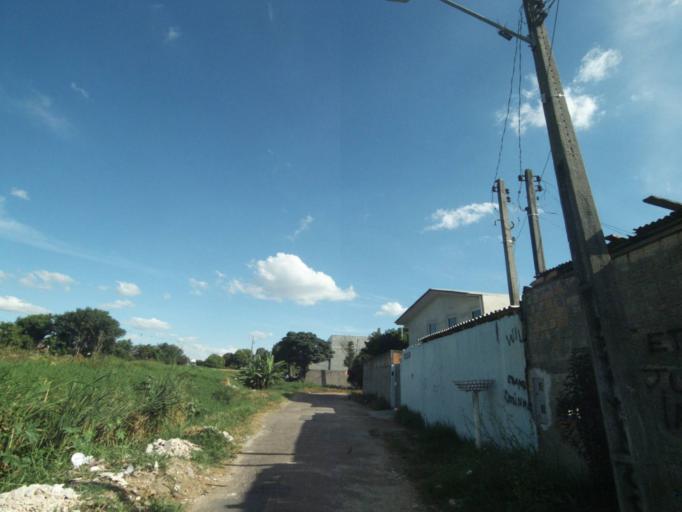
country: BR
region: Parana
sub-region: Pinhais
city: Pinhais
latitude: -25.4530
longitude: -49.2009
